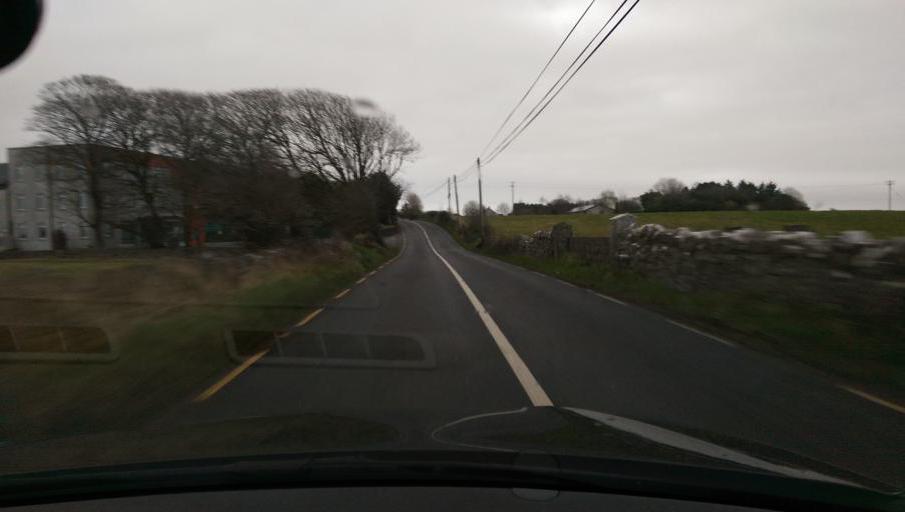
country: IE
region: Connaught
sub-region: County Galway
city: Athenry
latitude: 53.3091
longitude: -8.7926
